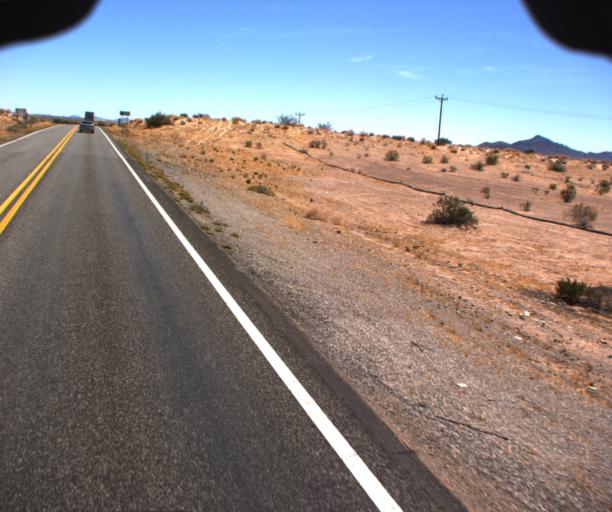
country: US
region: Arizona
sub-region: La Paz County
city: Parker
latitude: 34.0832
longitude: -114.2695
